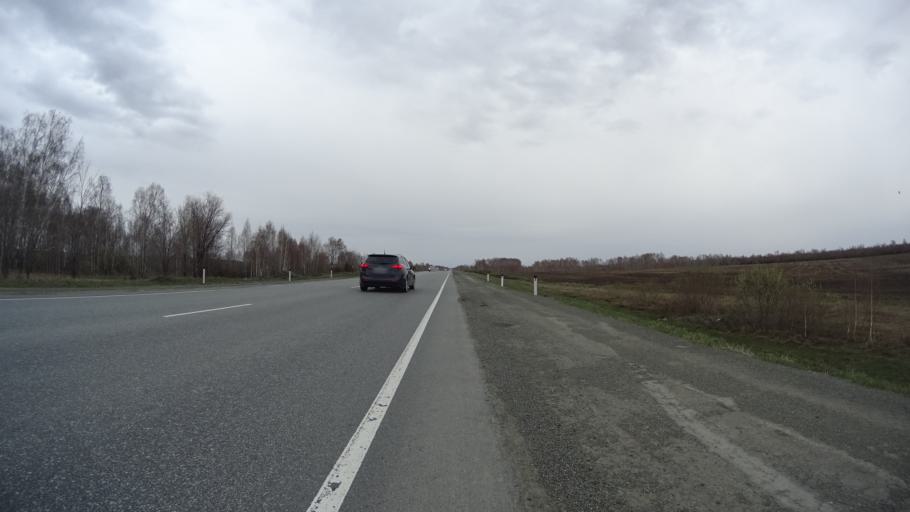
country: RU
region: Chelyabinsk
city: Krasnogorskiy
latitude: 54.6587
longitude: 61.2558
